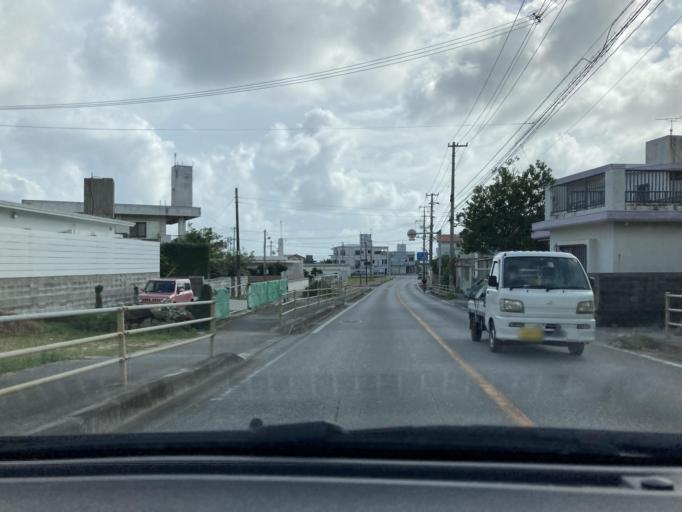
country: JP
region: Okinawa
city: Itoman
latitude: 26.0965
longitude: 127.6993
